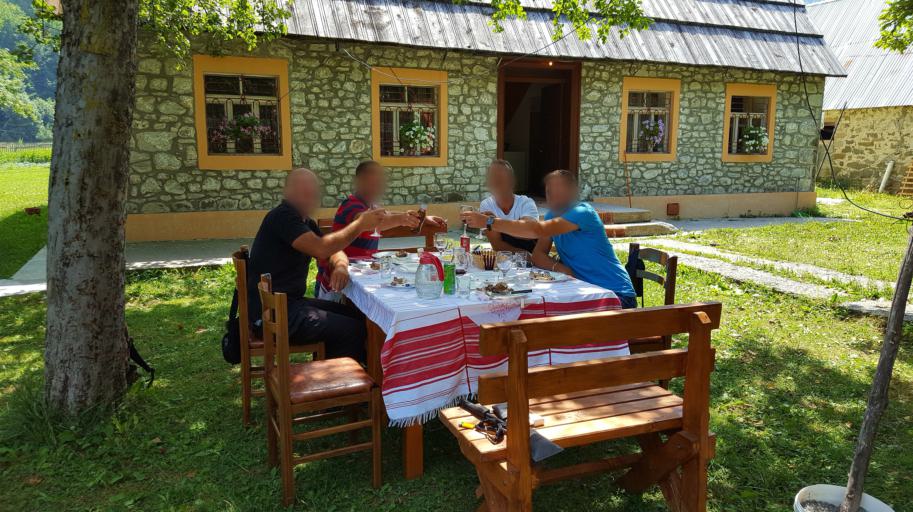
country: ME
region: Andrijevica
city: Andrijevica
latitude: 42.5919
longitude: 19.6856
